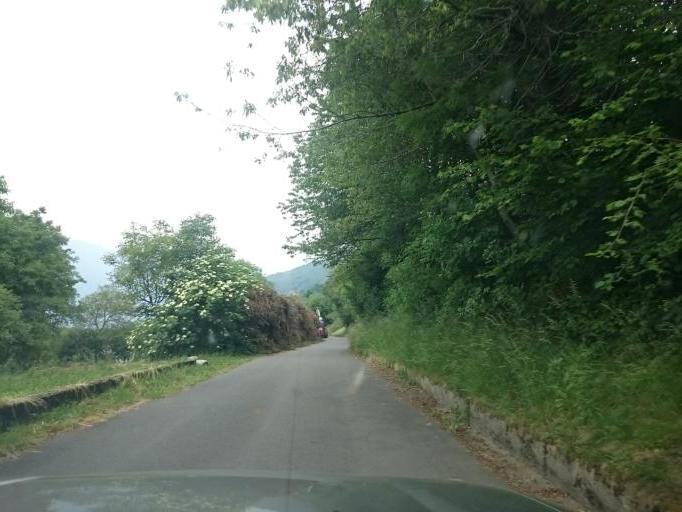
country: IT
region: Lombardy
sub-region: Provincia di Brescia
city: Cimbergo
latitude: 46.0194
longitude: 10.3691
